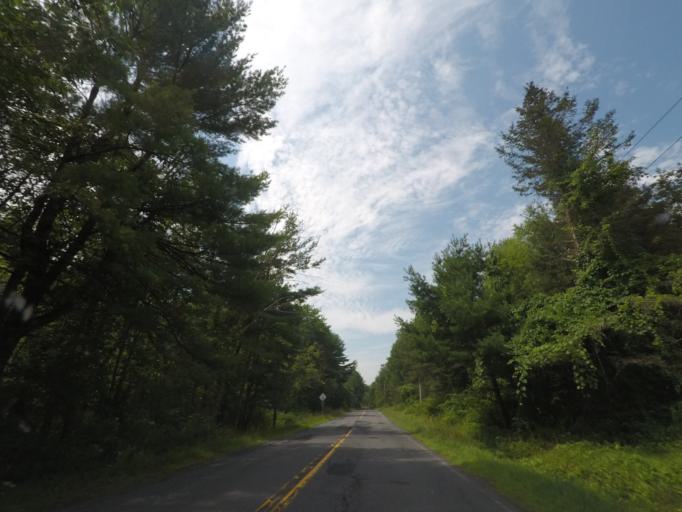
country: US
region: New York
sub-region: Rensselaer County
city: Wynantskill
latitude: 42.7454
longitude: -73.6046
